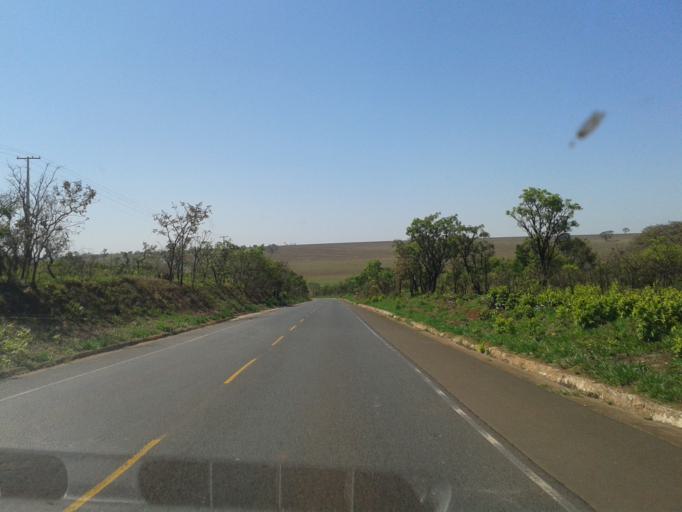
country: BR
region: Minas Gerais
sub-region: Uberlandia
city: Uberlandia
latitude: -19.1075
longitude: -47.9808
